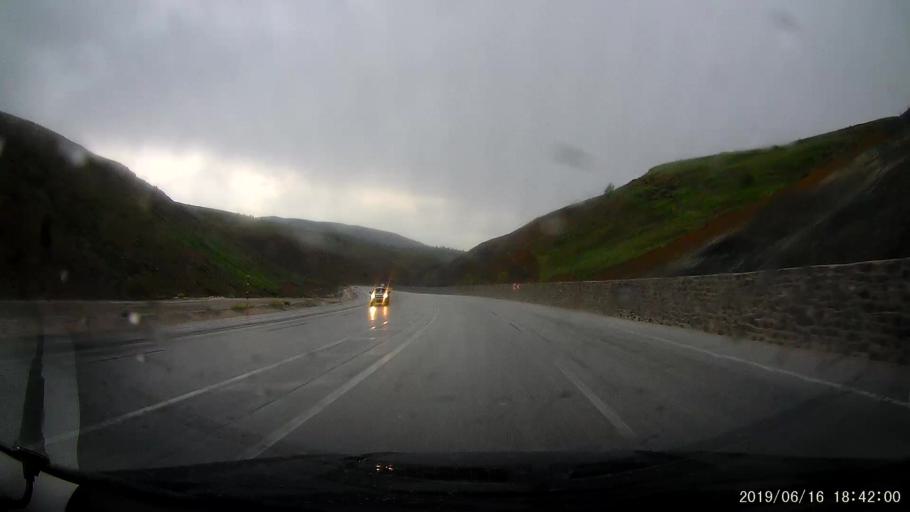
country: TR
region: Erzincan
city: Doganbeyli
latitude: 39.8726
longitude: 39.1176
